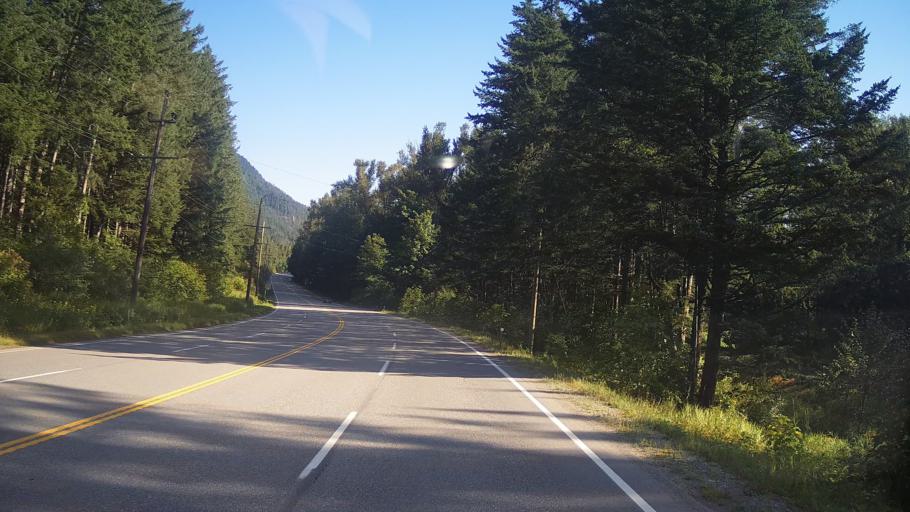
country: CA
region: British Columbia
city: Hope
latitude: 49.4415
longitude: -121.4364
